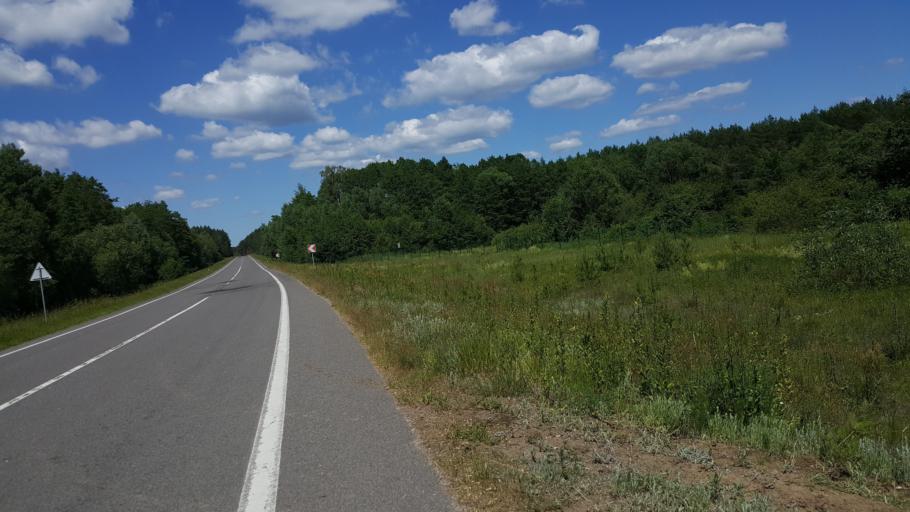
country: PL
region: Podlasie
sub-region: Powiat hajnowski
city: Czeremcha
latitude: 52.5155
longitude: 23.5339
